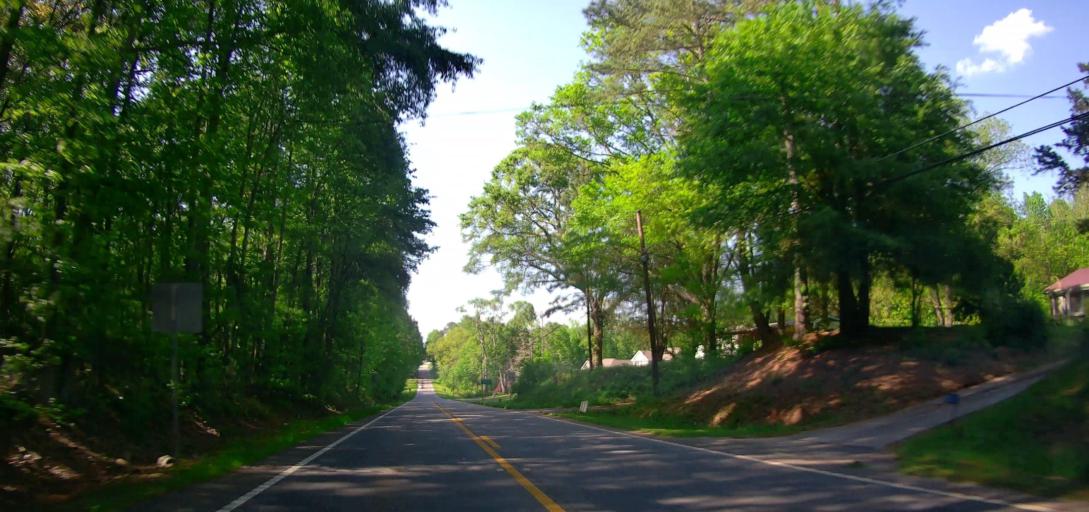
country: US
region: Georgia
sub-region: Morgan County
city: Madison
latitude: 33.6076
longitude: -83.4773
